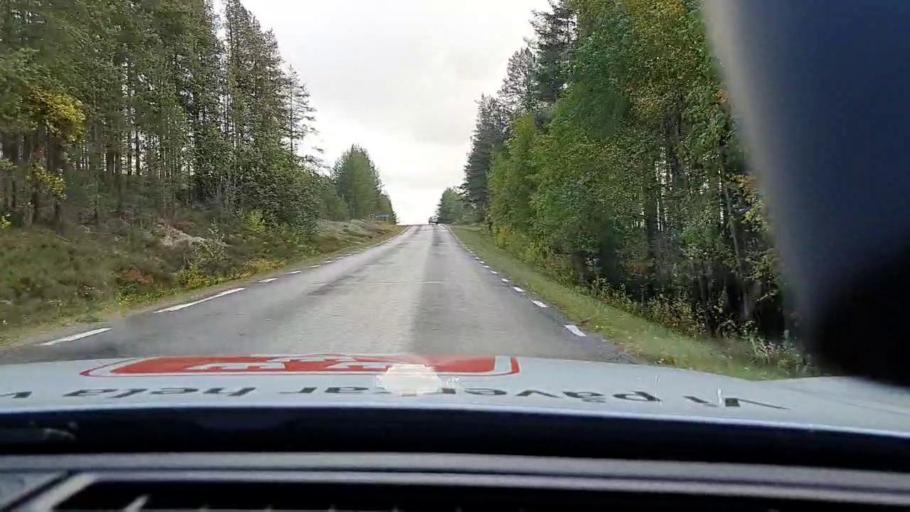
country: SE
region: Vaesterbotten
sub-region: Skelleftea Kommun
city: Langsele
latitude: 64.9602
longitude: 19.8994
